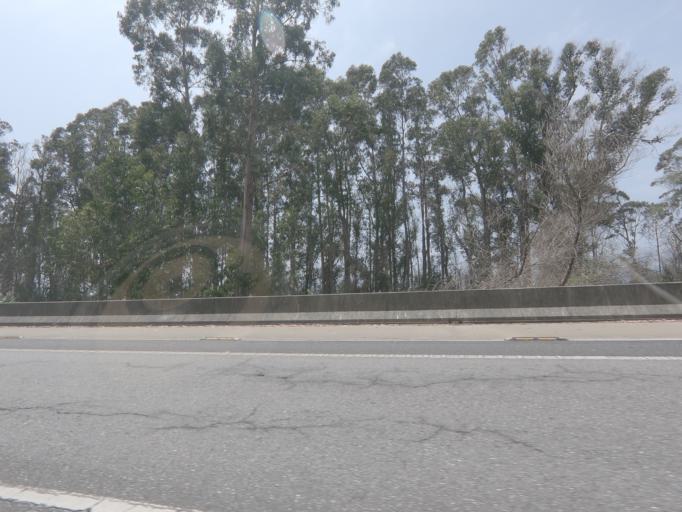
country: ES
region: Galicia
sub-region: Provincia de Pontevedra
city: A Guarda
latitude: 41.9262
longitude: -8.8811
